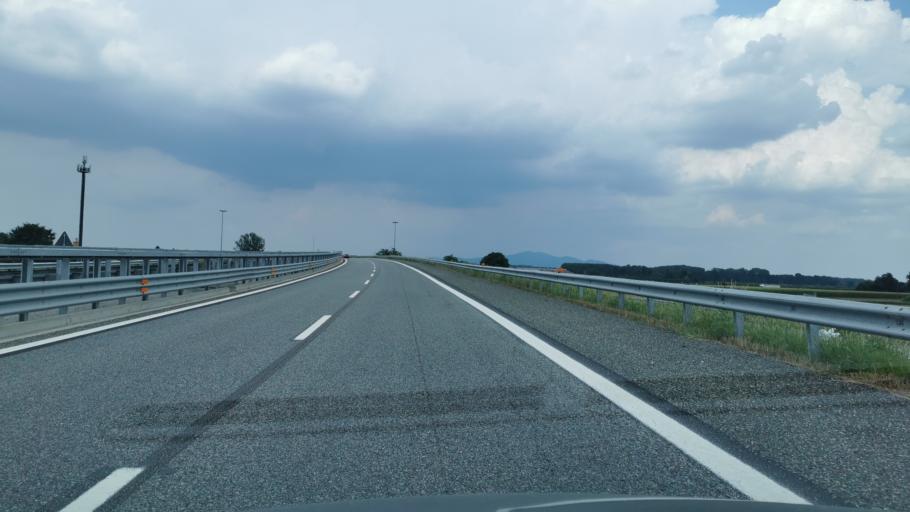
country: IT
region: Piedmont
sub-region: Provincia di Torino
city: Orbassano
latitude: 44.9782
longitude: 7.5490
